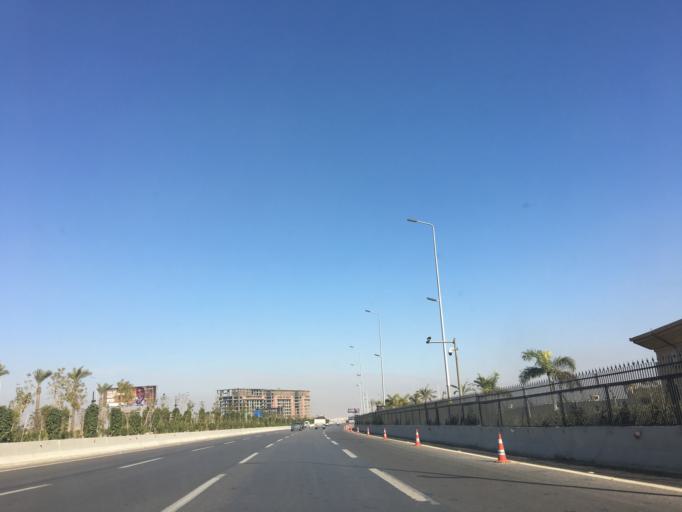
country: EG
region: Muhafazat al Qahirah
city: Cairo
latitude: 30.0421
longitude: 31.4051
